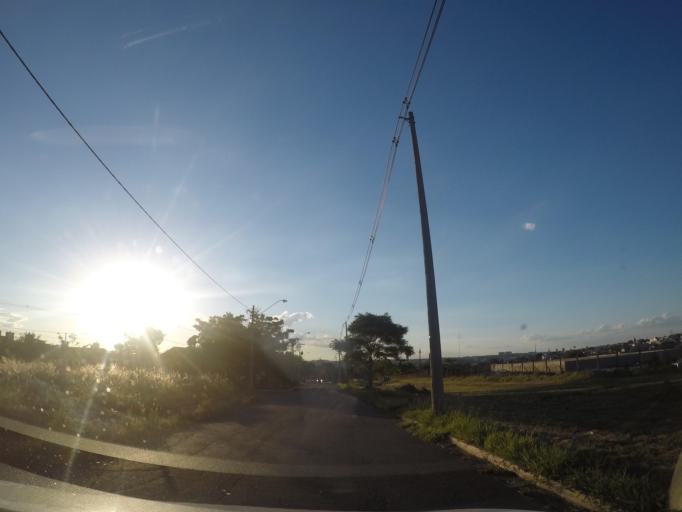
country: BR
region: Sao Paulo
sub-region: Sumare
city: Sumare
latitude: -22.8201
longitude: -47.2531
